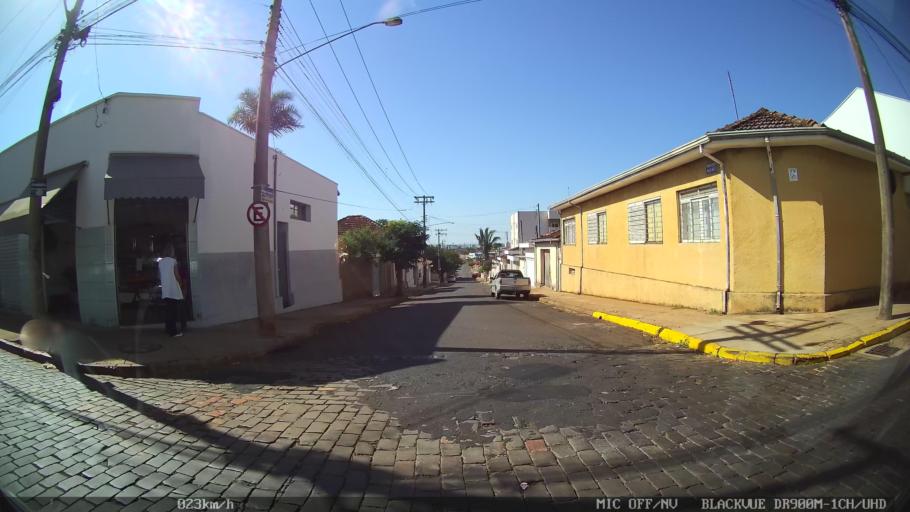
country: BR
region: Sao Paulo
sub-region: Batatais
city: Batatais
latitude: -20.8966
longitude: -47.5838
